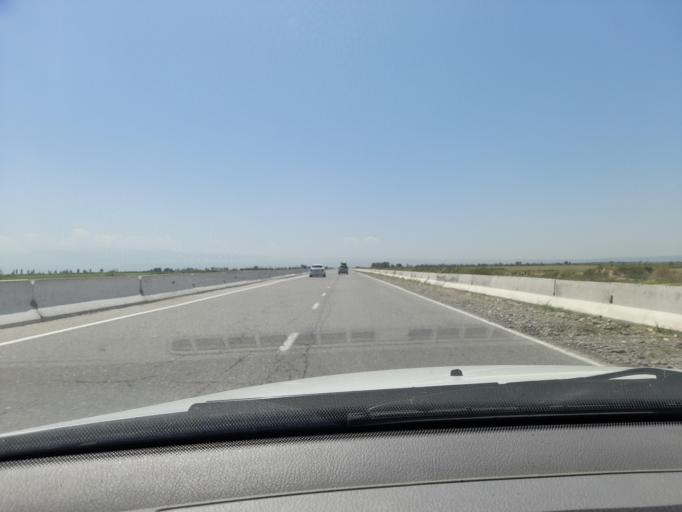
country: UZ
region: Jizzax
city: Paxtakor
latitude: 40.2232
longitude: 67.9935
